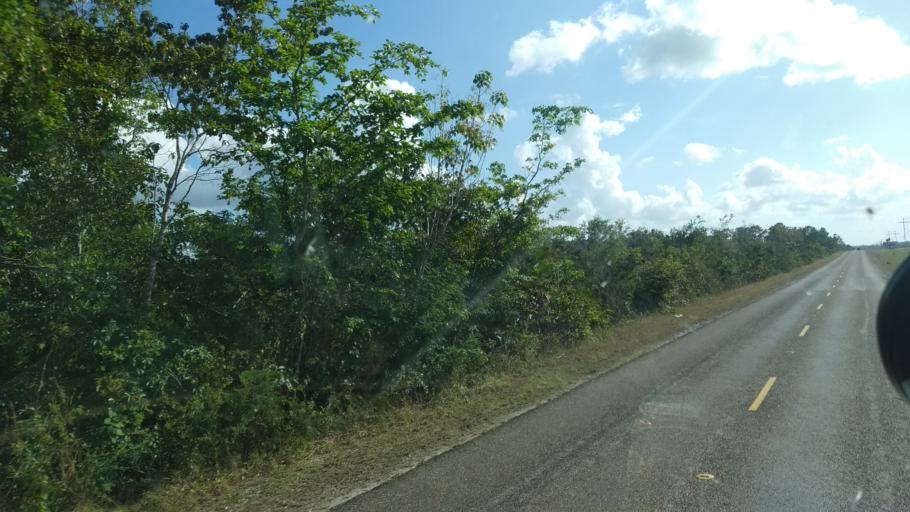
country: BZ
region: Cayo
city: Belmopan
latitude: 17.3715
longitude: -88.5324
